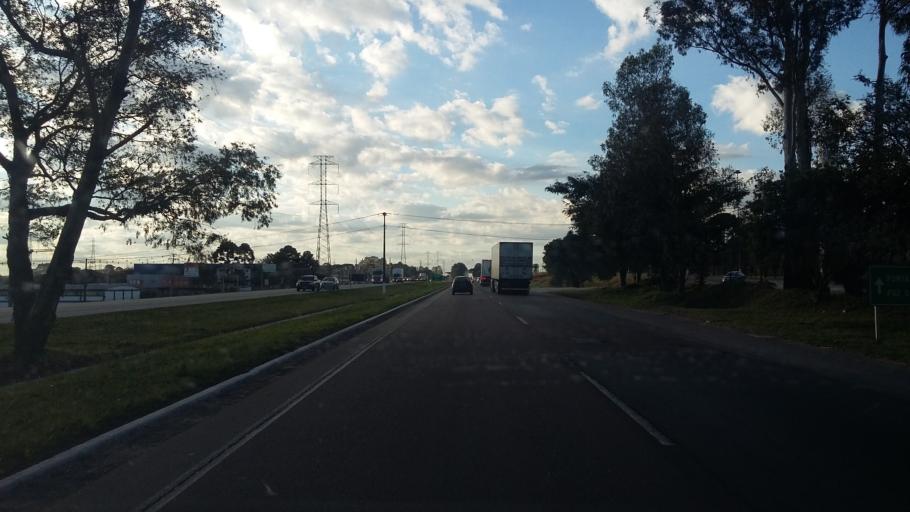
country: BR
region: Parana
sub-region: Curitiba
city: Curitiba
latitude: -25.4430
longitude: -49.3642
